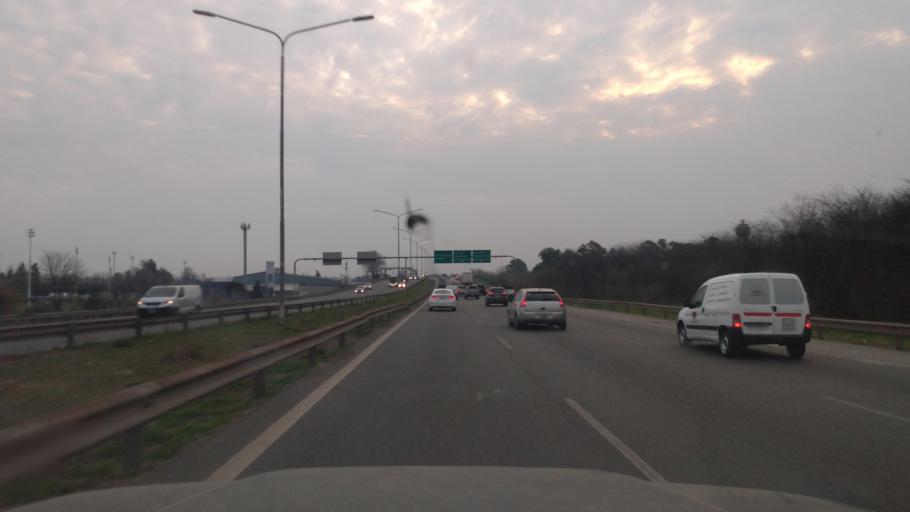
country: AR
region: Buenos Aires
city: Hurlingham
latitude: -34.5676
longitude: -58.6447
